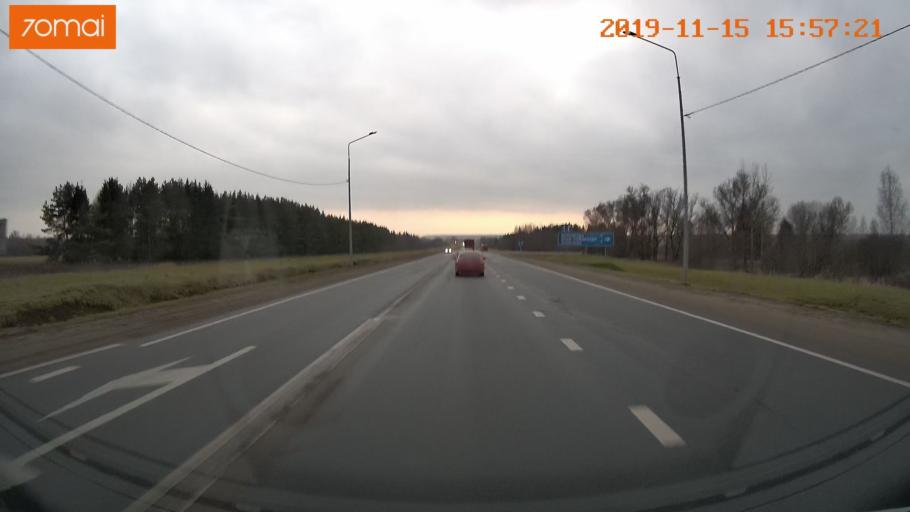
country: RU
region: Jaroslavl
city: Yaroslavl
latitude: 57.8312
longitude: 39.9643
